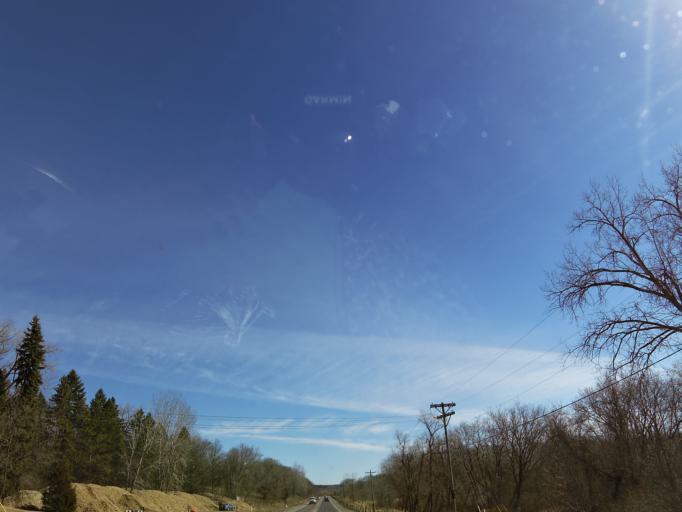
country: US
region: Minnesota
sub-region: Scott County
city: Shakopee
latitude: 44.8138
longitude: -93.5329
